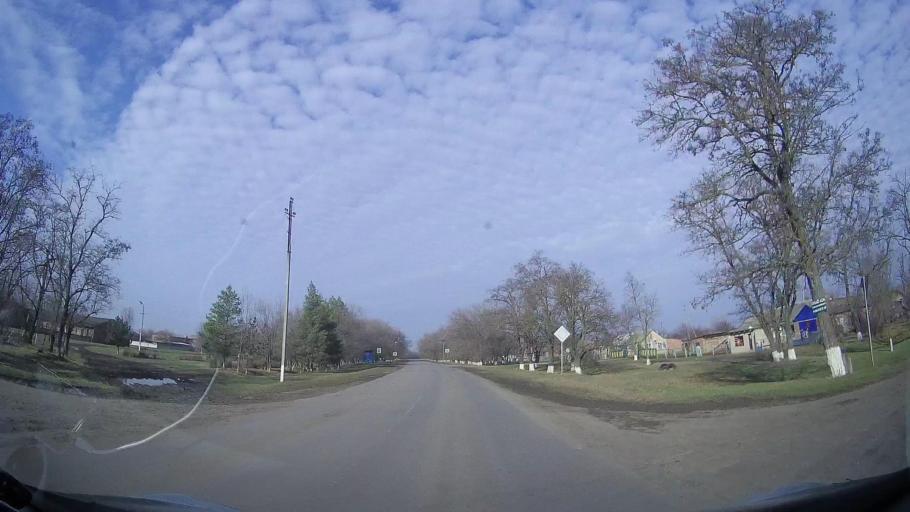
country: RU
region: Rostov
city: Gigant
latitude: 46.8353
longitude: 41.3339
